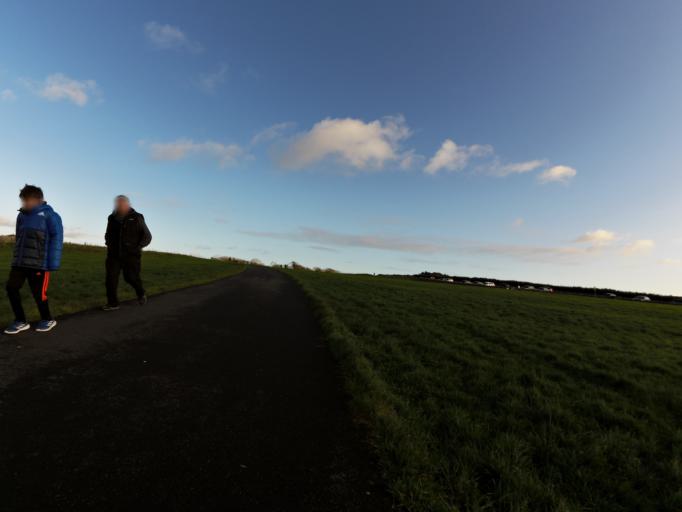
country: IE
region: Connaught
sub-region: County Galway
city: Oranmore
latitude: 53.2463
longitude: -8.9596
